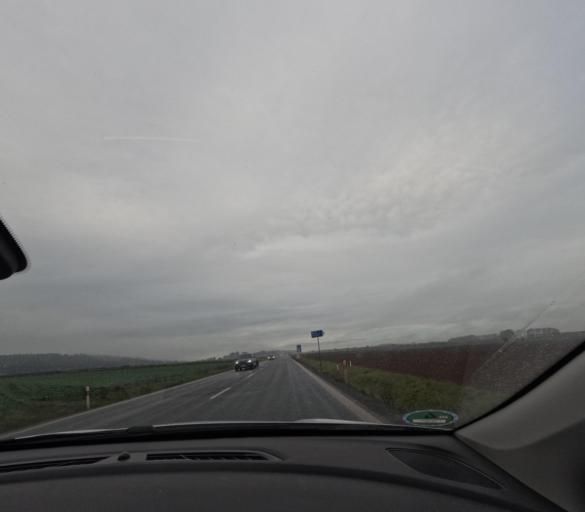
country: CZ
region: Central Bohemia
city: Rakovnik
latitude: 50.1706
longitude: 13.7032
